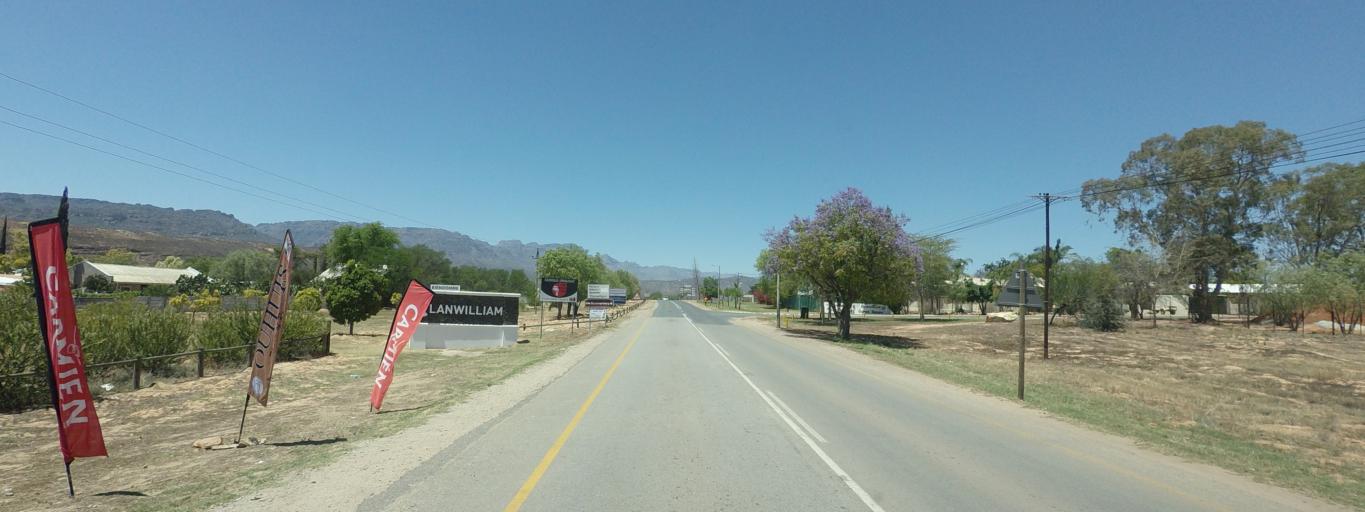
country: ZA
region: Western Cape
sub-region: West Coast District Municipality
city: Clanwilliam
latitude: -32.1736
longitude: 18.8862
